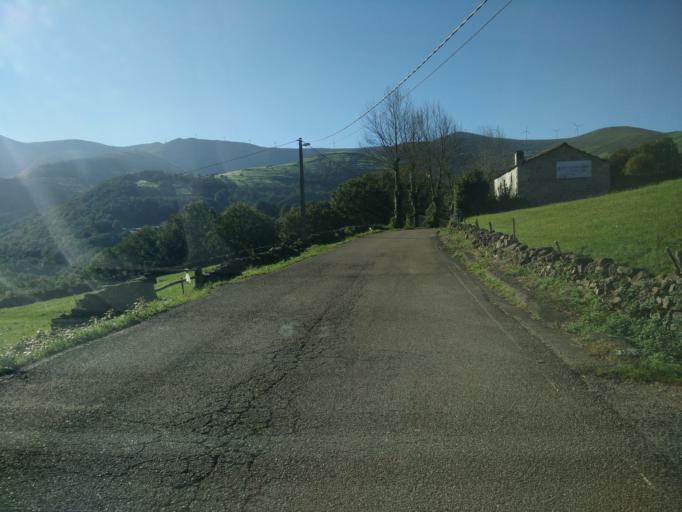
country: ES
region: Cantabria
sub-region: Provincia de Cantabria
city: San Pedro del Romeral
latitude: 43.1150
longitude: -3.8074
